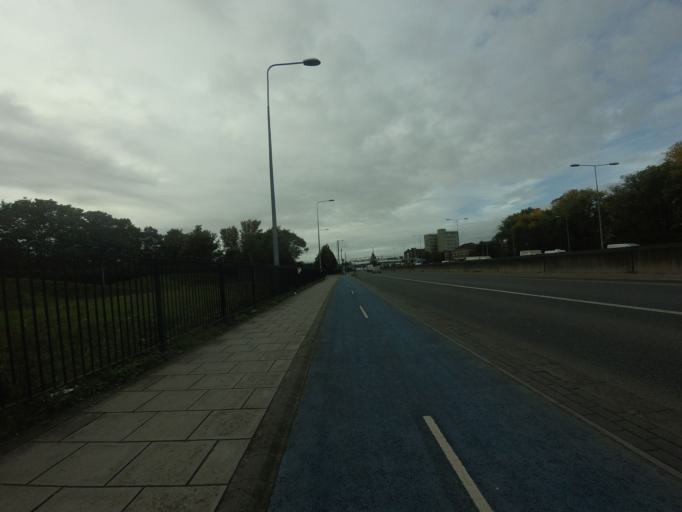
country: GB
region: England
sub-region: Greater London
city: Barking
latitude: 51.5295
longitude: 0.0915
